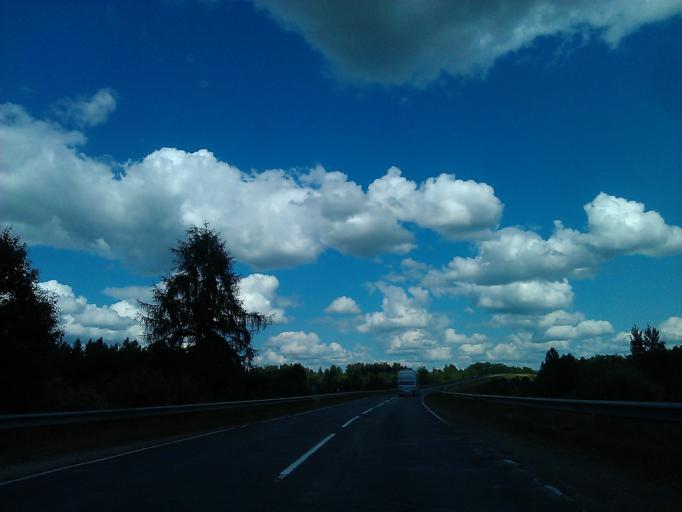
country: LV
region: Rezekne
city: Rezekne
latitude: 56.5481
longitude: 27.3156
